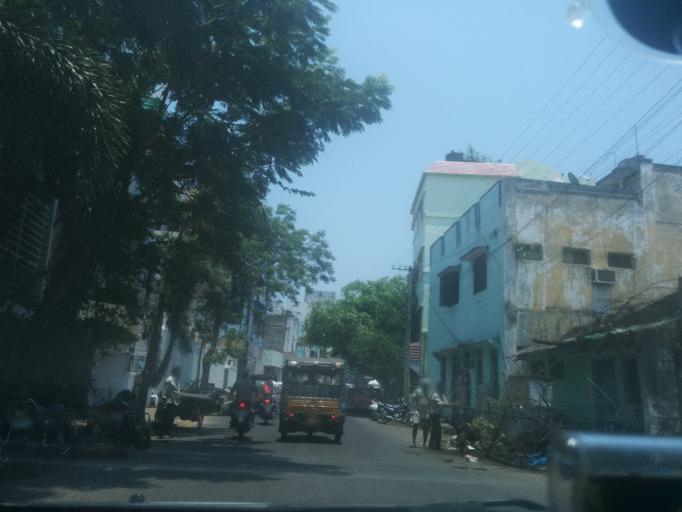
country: IN
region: Andhra Pradesh
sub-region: East Godavari
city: Rajahmundry
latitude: 16.9980
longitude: 81.7752
